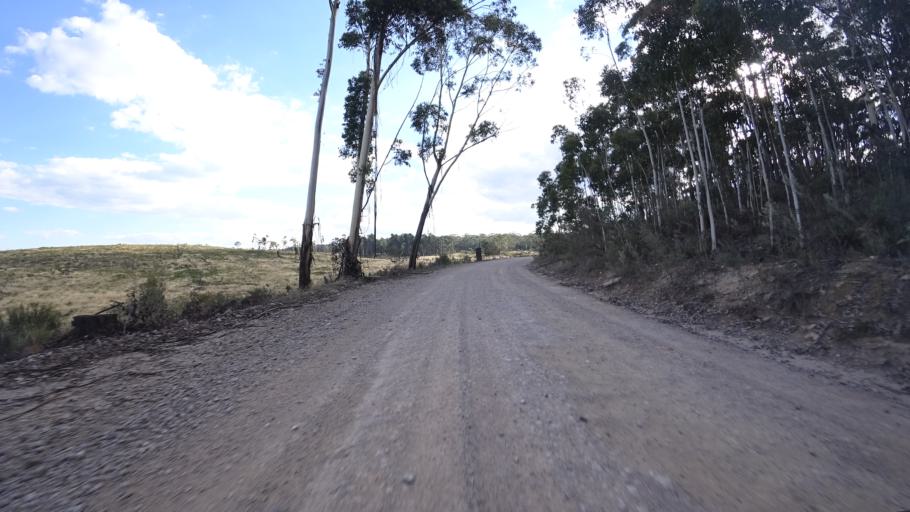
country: AU
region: New South Wales
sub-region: Lithgow
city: Lithgow
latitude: -33.3997
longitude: 150.2045
